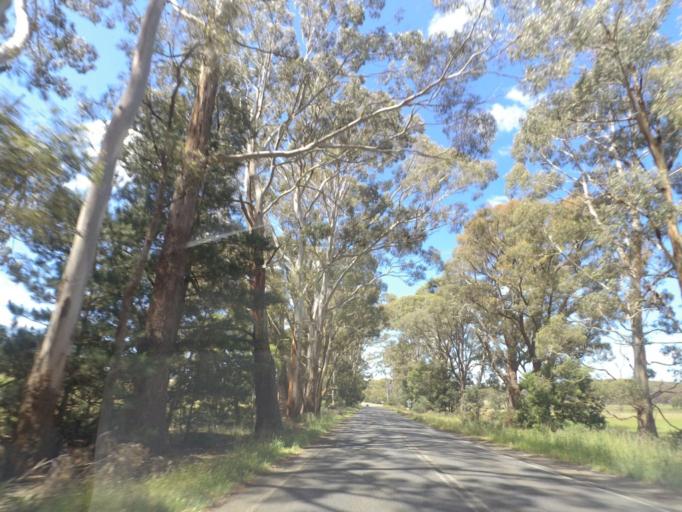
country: AU
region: Victoria
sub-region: Mount Alexander
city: Castlemaine
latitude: -37.3157
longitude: 144.2216
